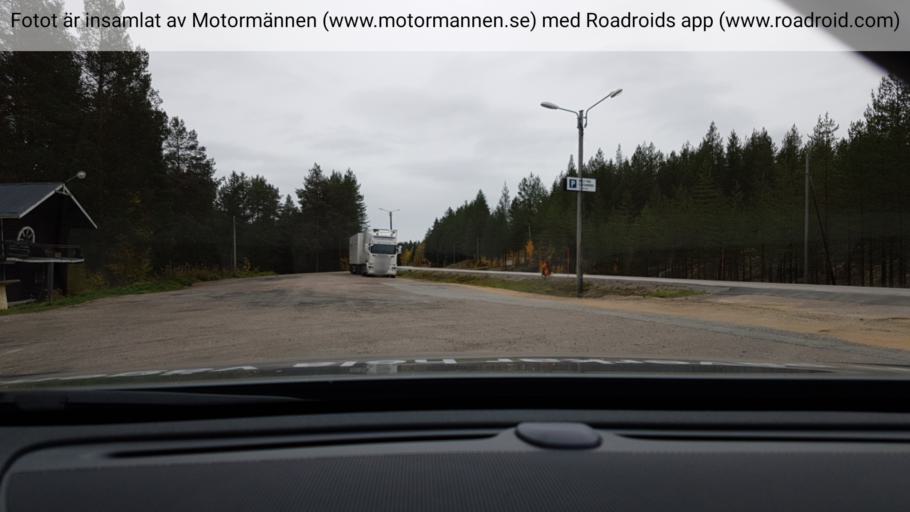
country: SE
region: Norrbotten
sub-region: Overkalix Kommun
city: OEverkalix
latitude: 66.2942
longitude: 22.8182
